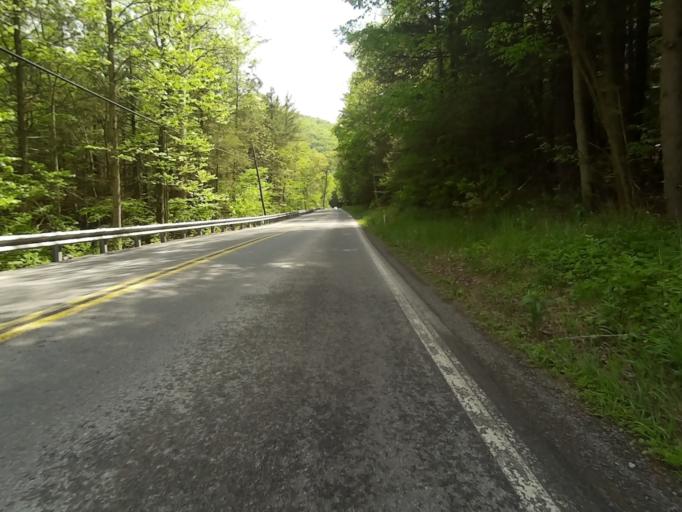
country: US
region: Pennsylvania
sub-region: Centre County
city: Zion
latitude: 41.0035
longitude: -77.6434
